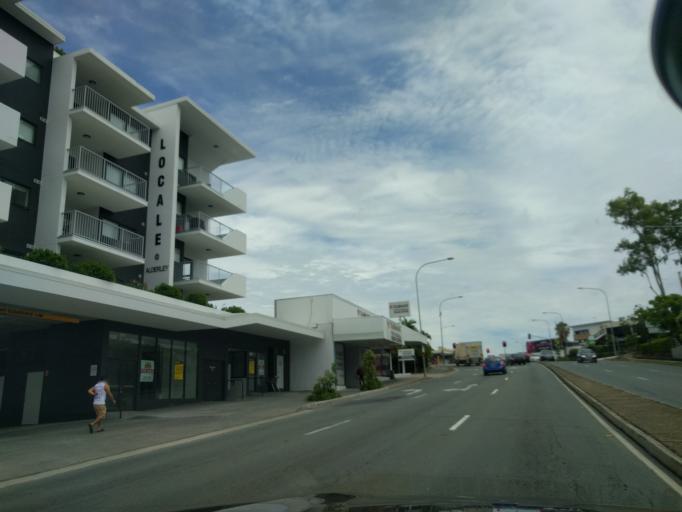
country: AU
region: Queensland
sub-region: Brisbane
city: Grange
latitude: -27.4262
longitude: 153.0017
